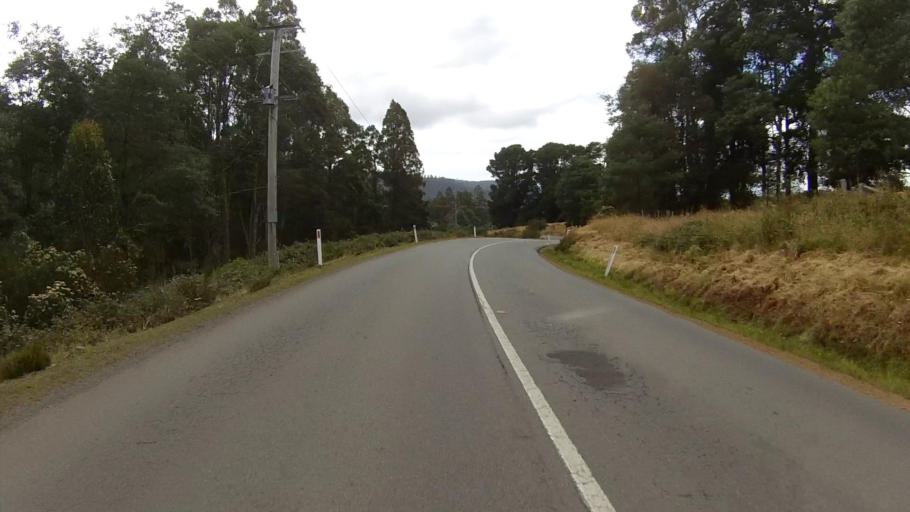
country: AU
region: Tasmania
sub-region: Kingborough
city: Kettering
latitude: -43.1134
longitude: 147.1932
